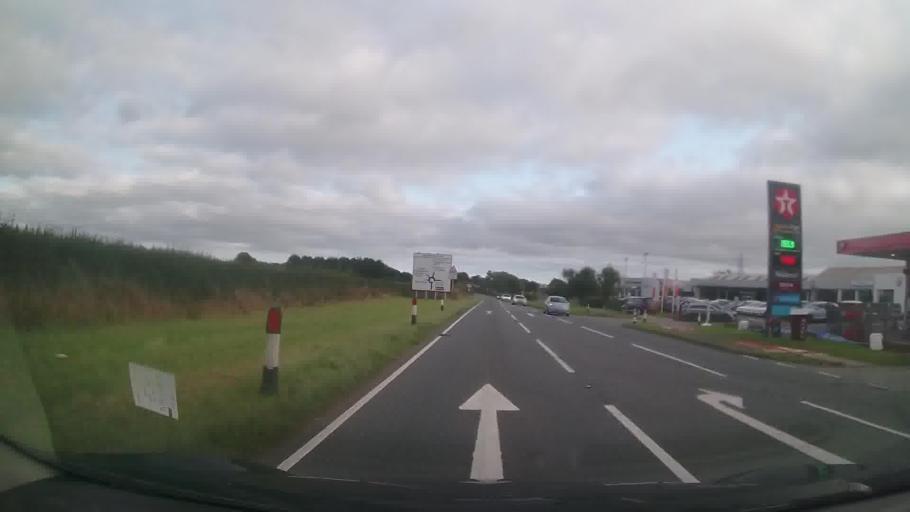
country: GB
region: Wales
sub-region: Pembrokeshire
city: Neyland
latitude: 51.7197
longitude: -4.9632
